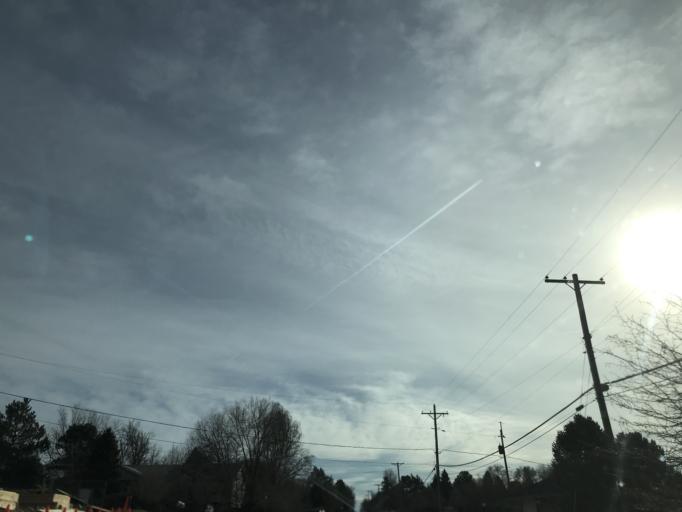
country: US
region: Colorado
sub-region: Arapahoe County
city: Littleton
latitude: 39.6017
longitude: -105.0187
